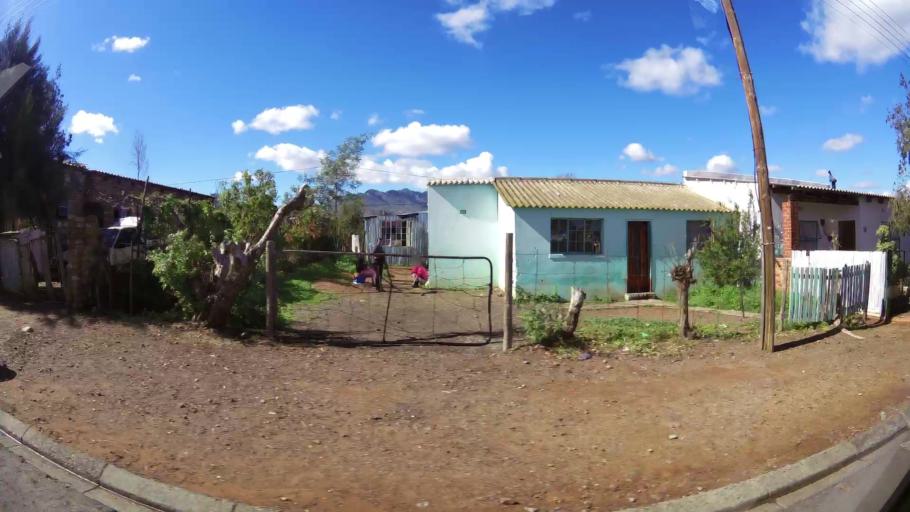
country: ZA
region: Western Cape
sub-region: Cape Winelands District Municipality
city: Ashton
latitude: -33.8345
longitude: 20.0434
